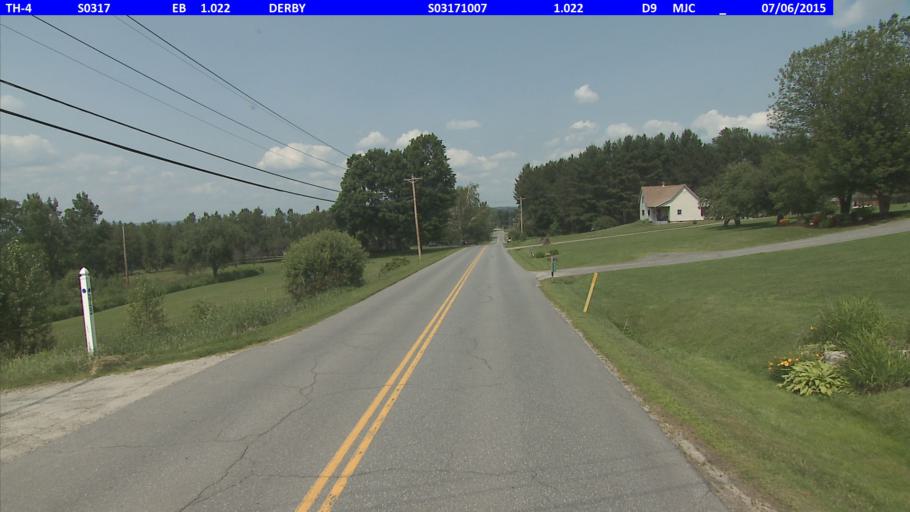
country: US
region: Vermont
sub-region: Orleans County
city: Newport
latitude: 44.9631
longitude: -72.1825
